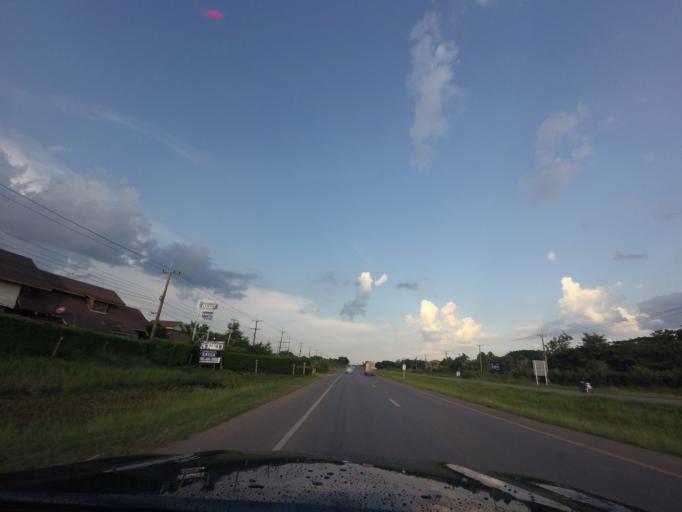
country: TH
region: Khon Kaen
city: Khon Kaen
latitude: 16.3968
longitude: 102.8595
